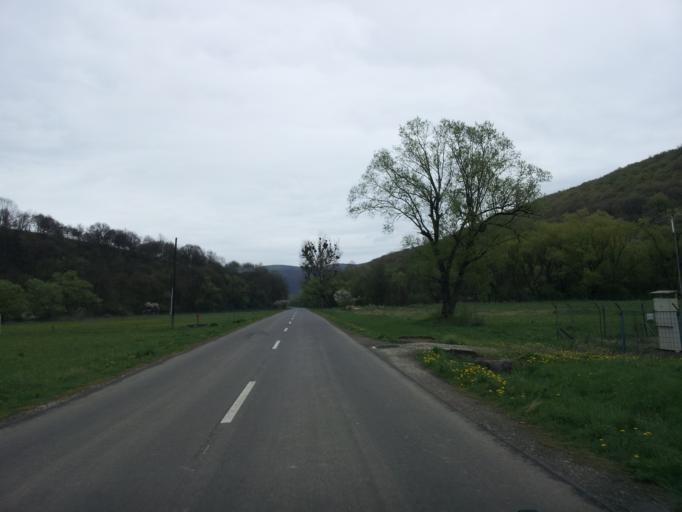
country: HU
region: Borsod-Abauj-Zemplen
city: Szendro
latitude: 48.4983
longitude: 20.6704
